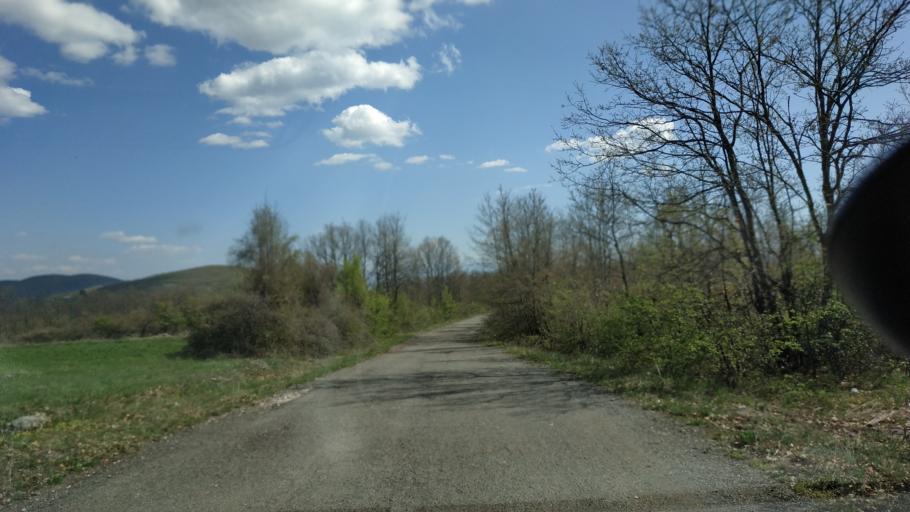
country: RS
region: Central Serbia
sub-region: Zajecarski Okrug
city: Soko Banja
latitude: 43.5432
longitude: 21.9024
